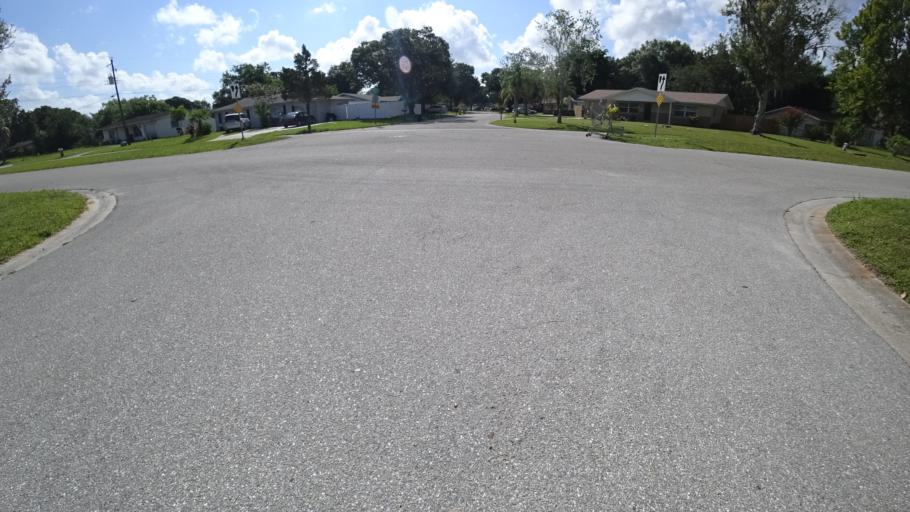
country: US
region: Florida
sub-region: Manatee County
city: Ellenton
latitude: 27.4959
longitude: -82.4803
